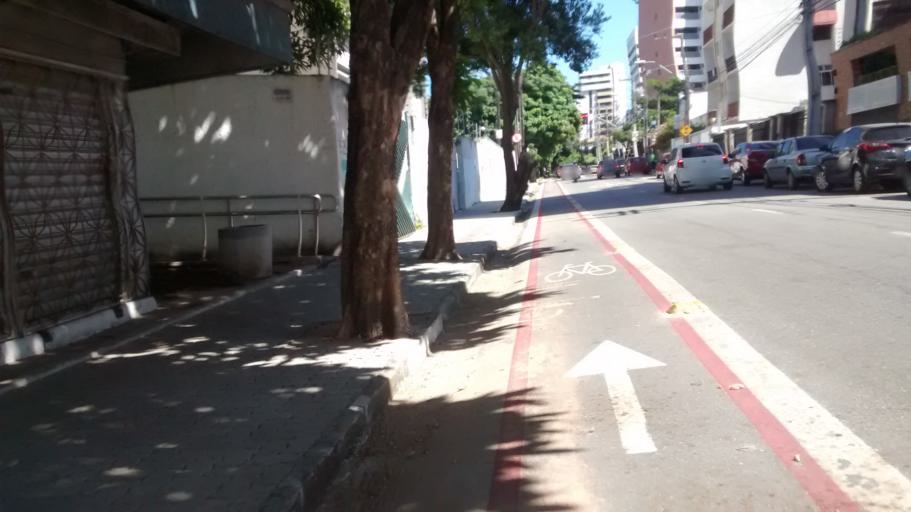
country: BR
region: Ceara
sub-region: Fortaleza
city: Fortaleza
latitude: -3.7426
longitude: -38.5026
